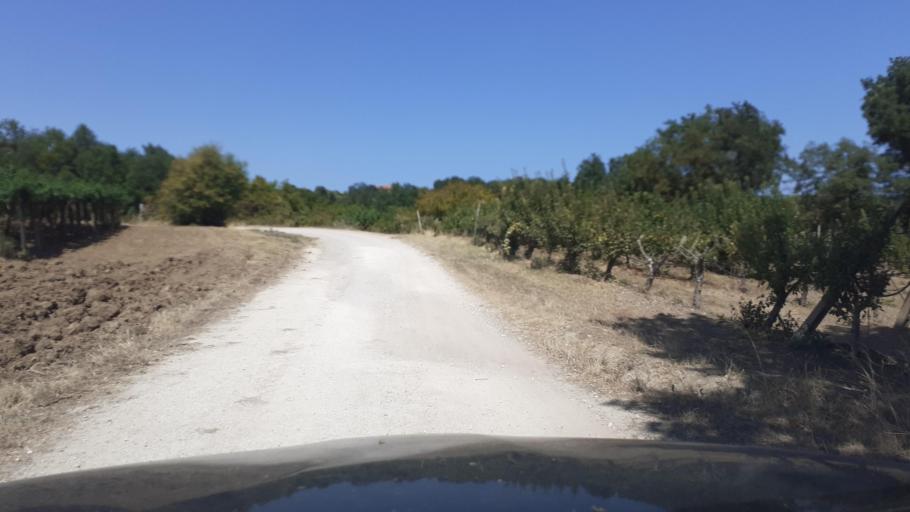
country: IT
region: Abruzzo
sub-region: Provincia di Chieti
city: Santa Maria Imbaro
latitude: 42.2086
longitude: 14.4772
